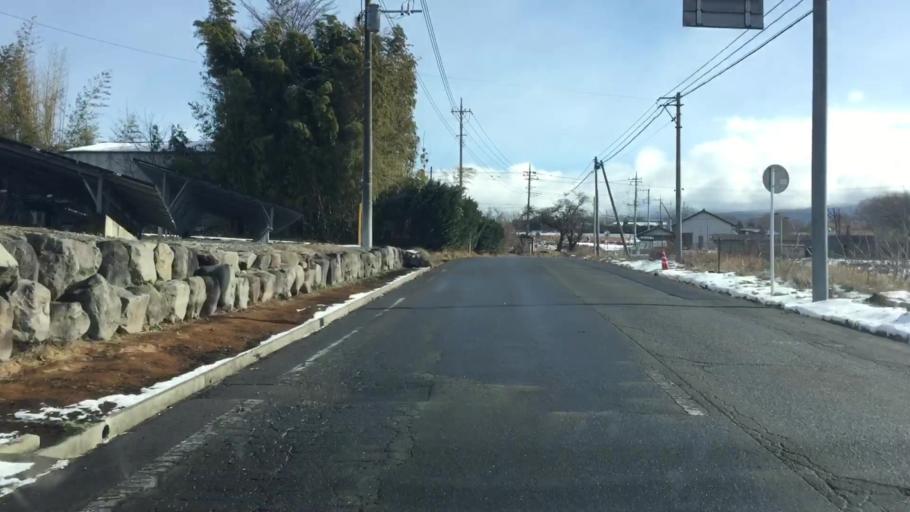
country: JP
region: Gunma
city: Numata
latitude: 36.6074
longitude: 139.0897
